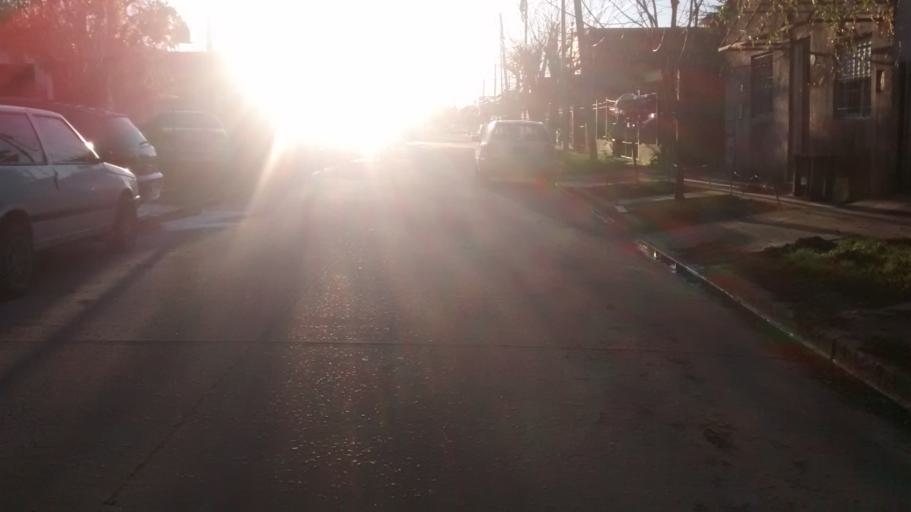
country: AR
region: Buenos Aires
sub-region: Partido de La Plata
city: La Plata
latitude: -34.9594
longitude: -57.9467
